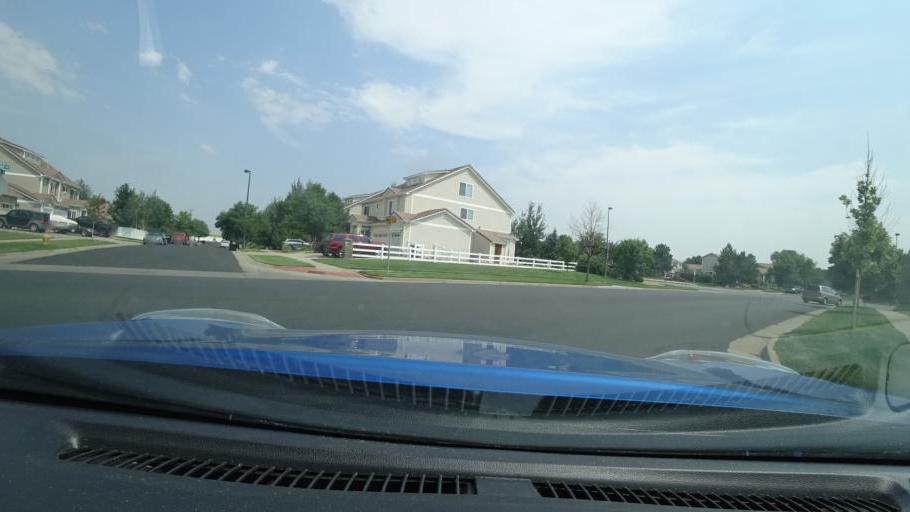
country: US
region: Colorado
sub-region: Adams County
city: Aurora
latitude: 39.7824
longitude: -104.7371
